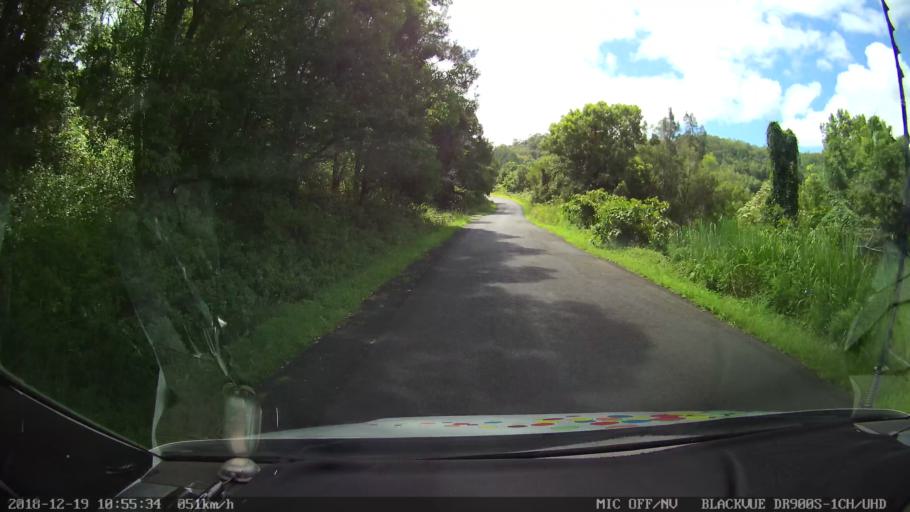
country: AU
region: New South Wales
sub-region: Lismore Municipality
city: Nimbin
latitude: -28.5953
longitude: 153.2553
